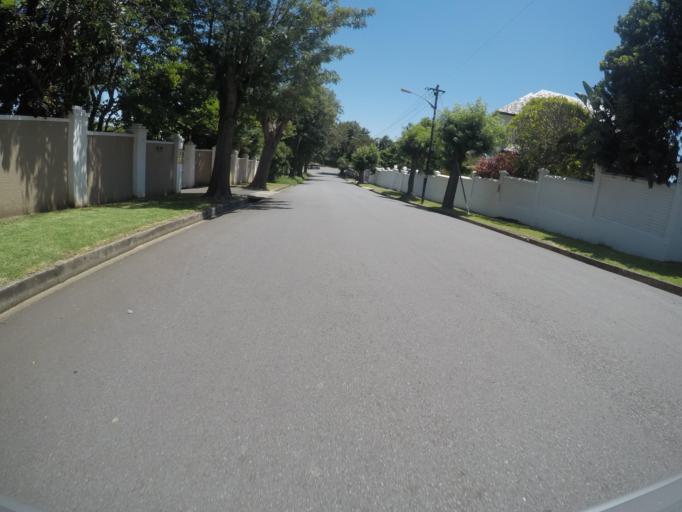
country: ZA
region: Eastern Cape
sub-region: Buffalo City Metropolitan Municipality
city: East London
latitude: -32.9878
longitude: 27.8975
